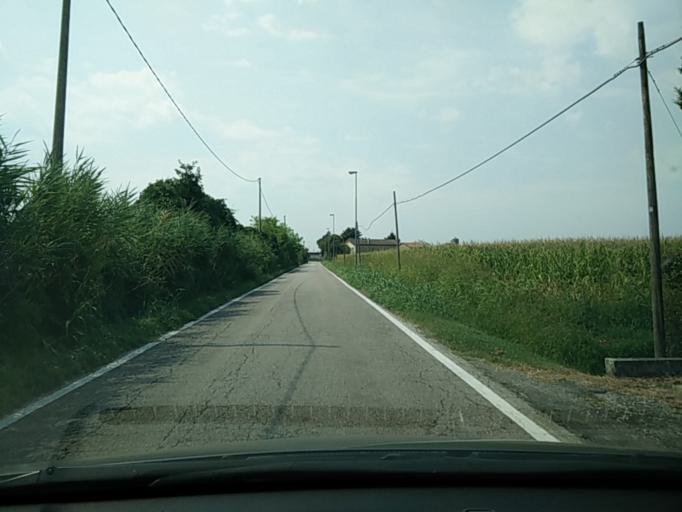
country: IT
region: Veneto
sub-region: Provincia di Venezia
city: Eraclea
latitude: 45.5653
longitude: 12.6495
